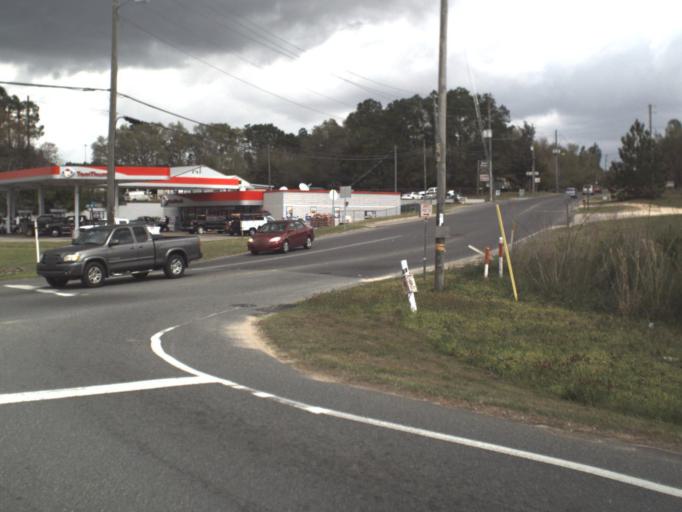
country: US
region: Florida
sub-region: Okaloosa County
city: Crestview
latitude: 30.7204
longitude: -86.5692
